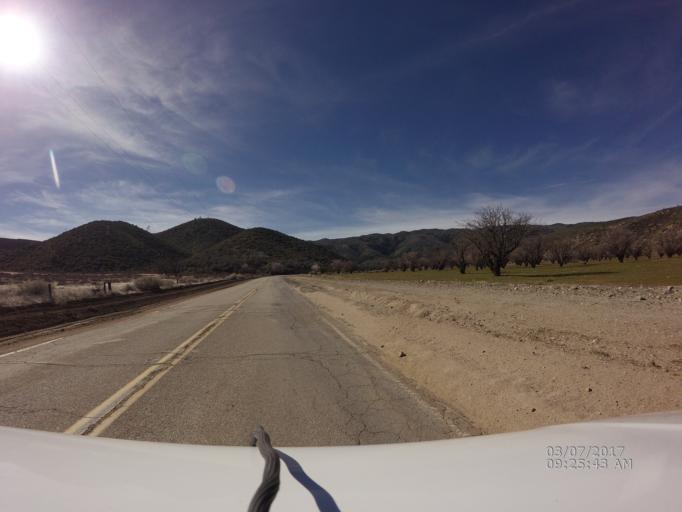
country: US
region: California
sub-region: Los Angeles County
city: Green Valley
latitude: 34.7460
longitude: -118.5985
